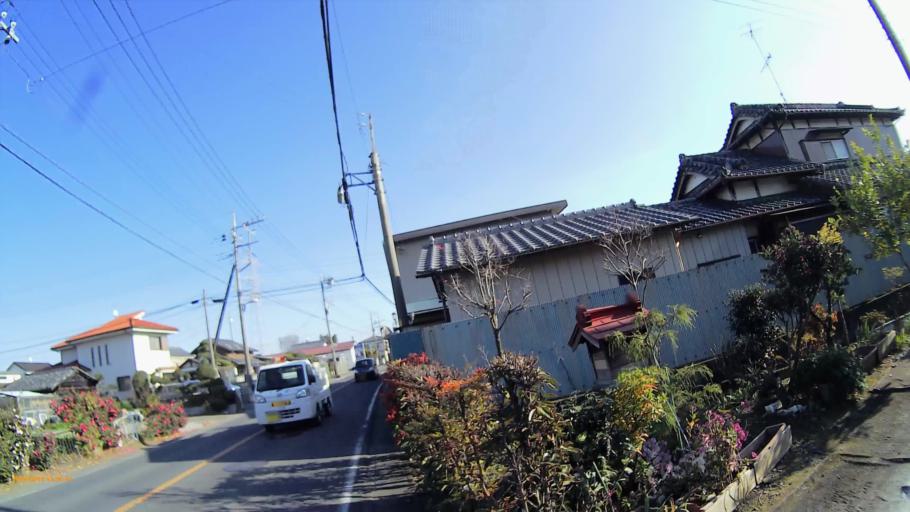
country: JP
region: Saitama
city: Konosu
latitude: 36.0756
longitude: 139.4862
